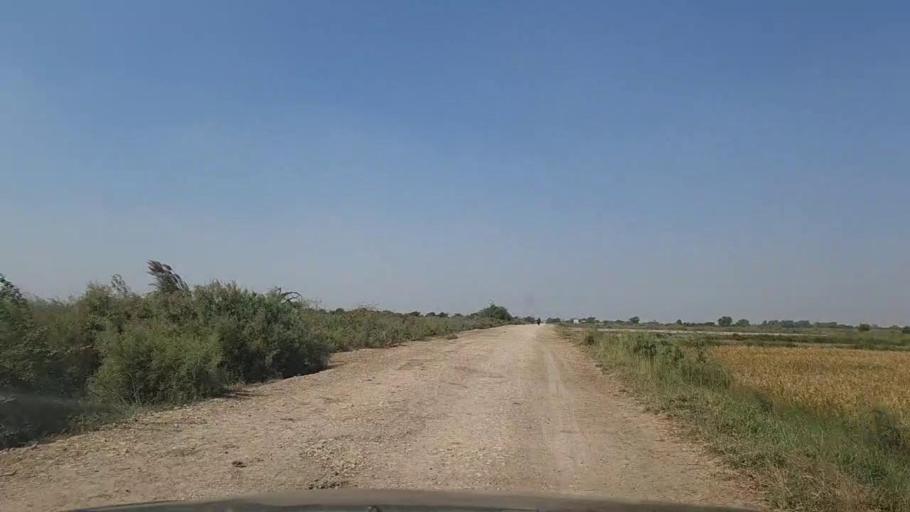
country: PK
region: Sindh
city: Daro Mehar
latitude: 24.8298
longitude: 68.1458
